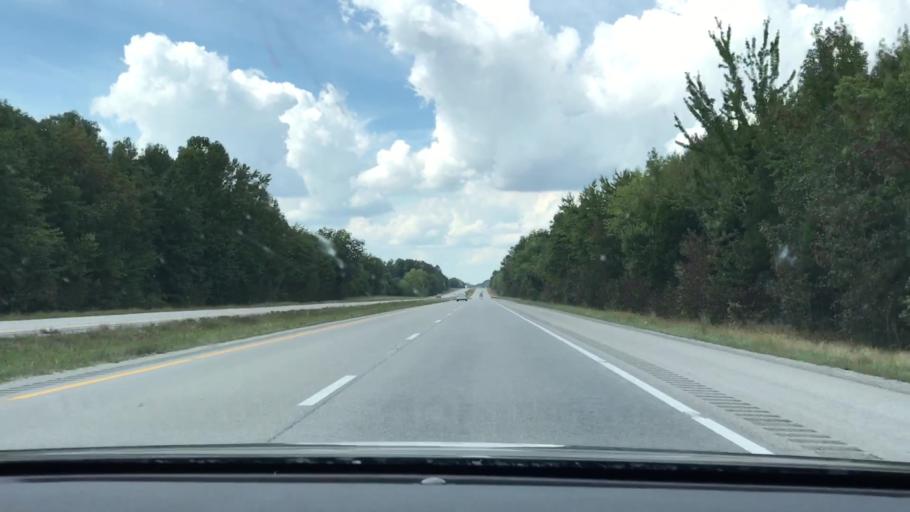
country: US
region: Kentucky
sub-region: Barren County
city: Glasgow
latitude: 37.0215
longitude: -86.0374
